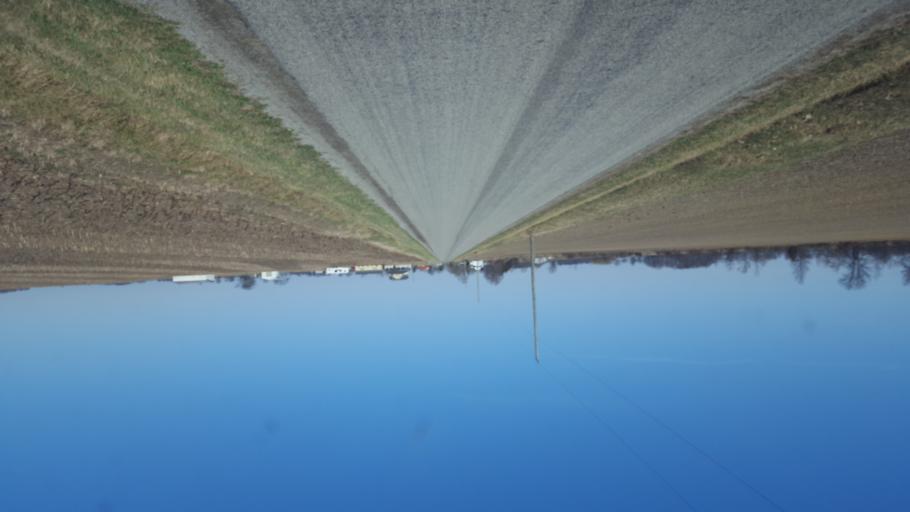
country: US
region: Ohio
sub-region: Union County
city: Richwood
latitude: 40.5007
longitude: -83.4357
